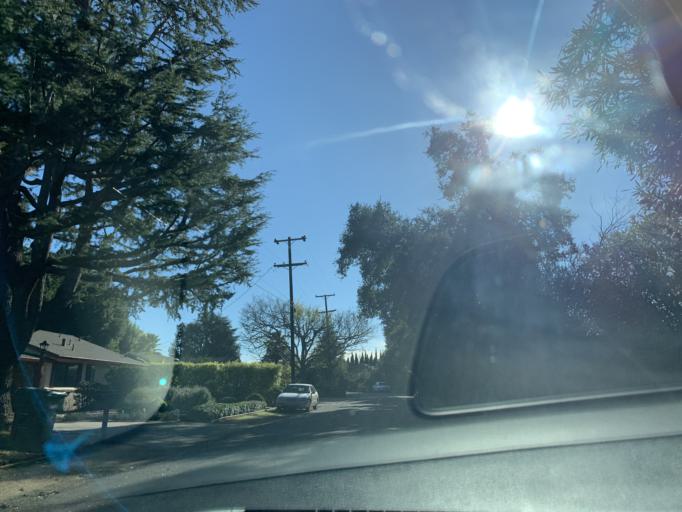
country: US
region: California
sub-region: Santa Clara County
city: Los Altos
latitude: 37.3832
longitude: -122.1039
